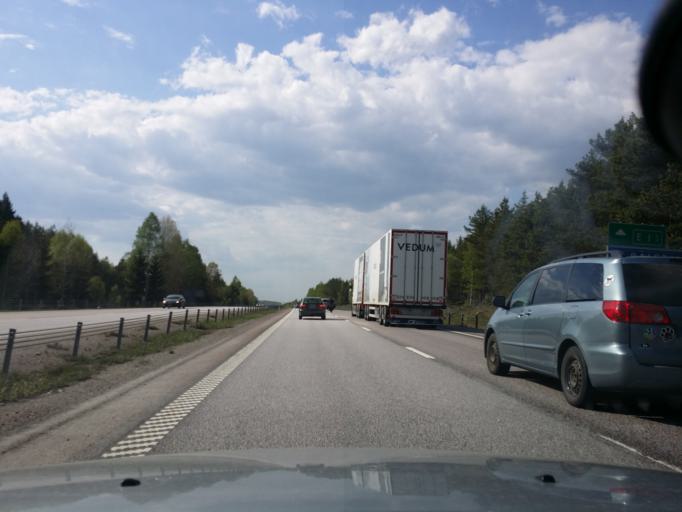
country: SE
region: Uppsala
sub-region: Habo Kommun
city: Balsta
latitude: 59.5603
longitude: 17.5737
